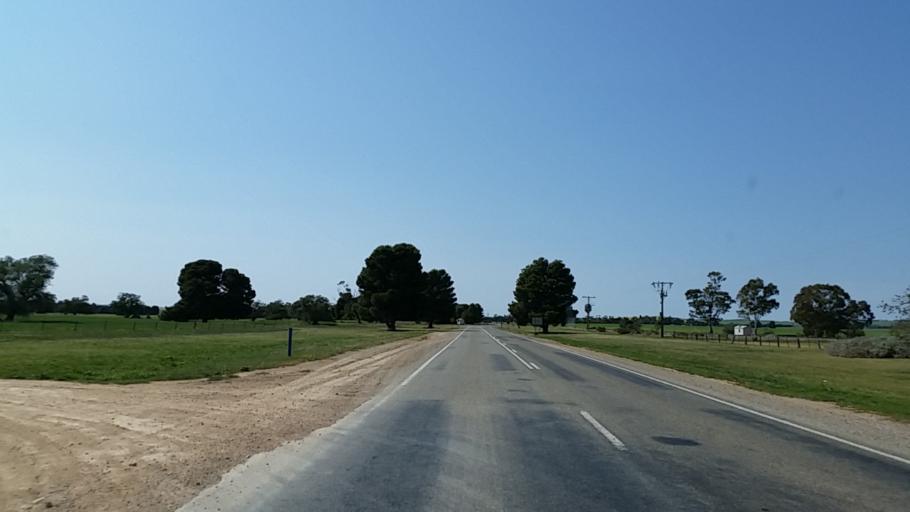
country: AU
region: South Australia
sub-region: Northern Areas
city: Jamestown
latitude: -33.1834
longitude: 138.4884
